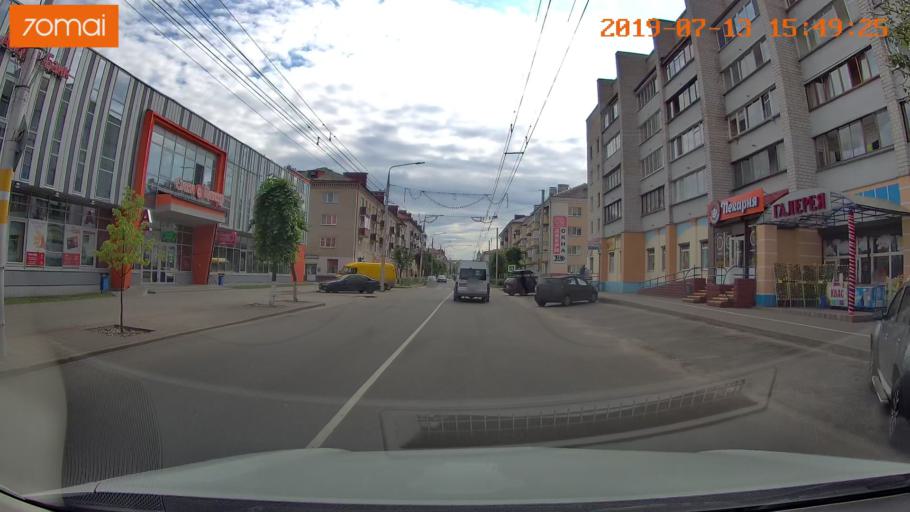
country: BY
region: Mogilev
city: Babruysk
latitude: 53.1470
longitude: 29.2291
